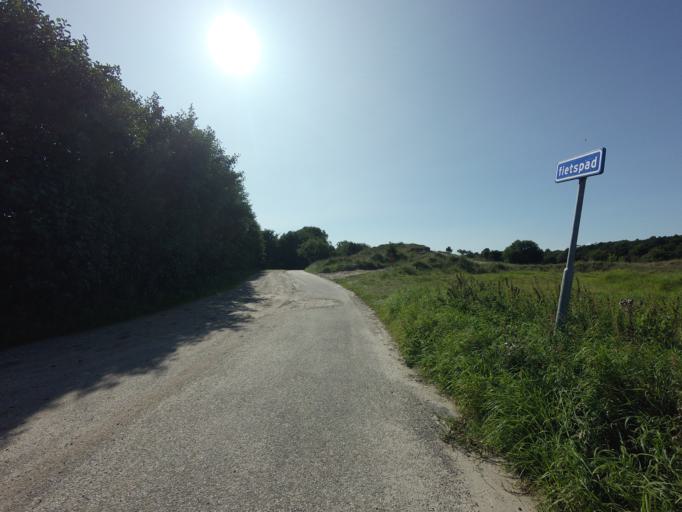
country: NL
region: Friesland
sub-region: Gemeente Terschelling
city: West-Terschelling
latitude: 53.3952
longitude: 5.3199
